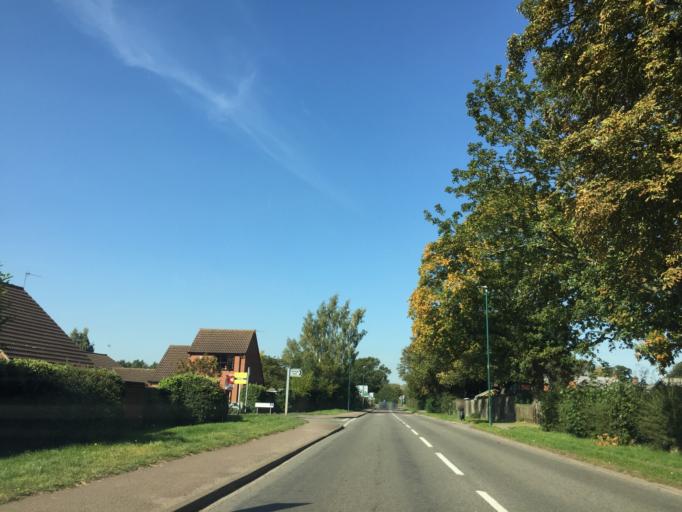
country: GB
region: England
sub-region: Leicestershire
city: Queniborough
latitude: 52.7070
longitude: -1.0498
